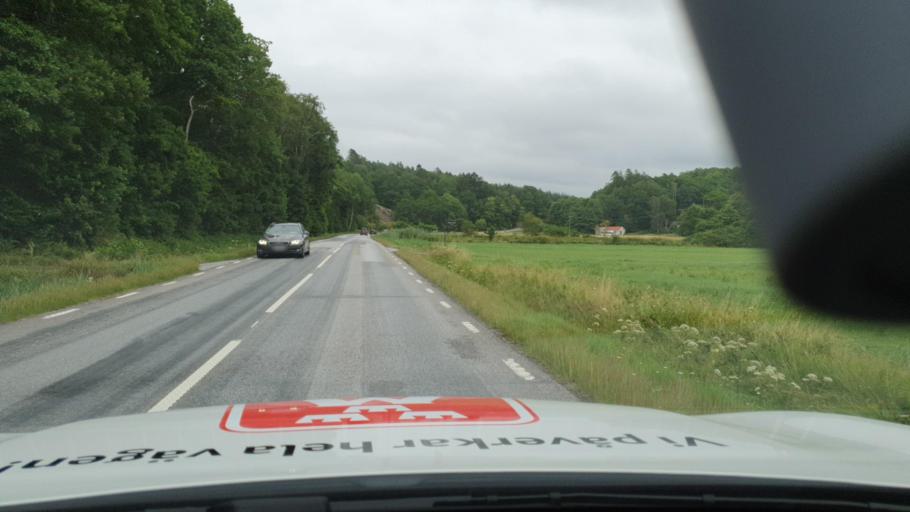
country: SE
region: Vaestra Goetaland
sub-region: Sotenas Kommun
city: Hunnebostrand
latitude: 58.4270
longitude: 11.3961
